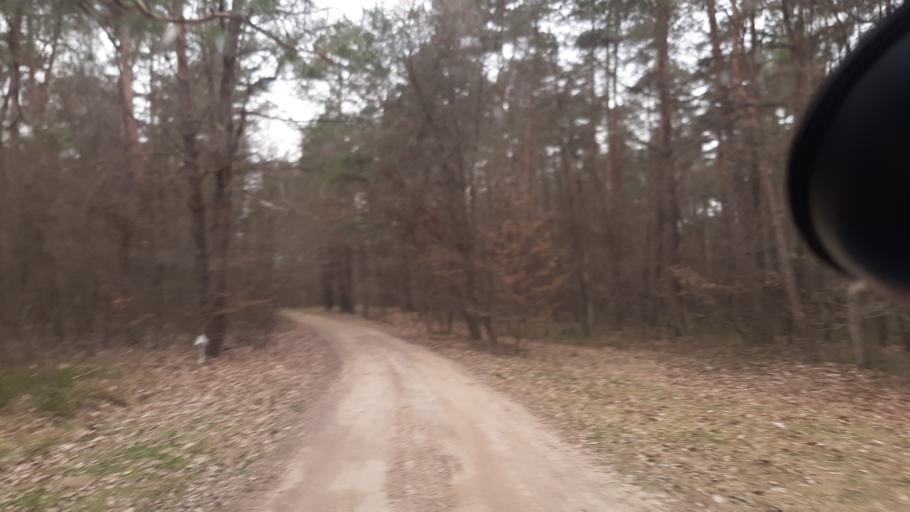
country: PL
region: Lublin Voivodeship
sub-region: Powiat lubartowski
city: Abramow
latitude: 51.4436
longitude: 22.3439
